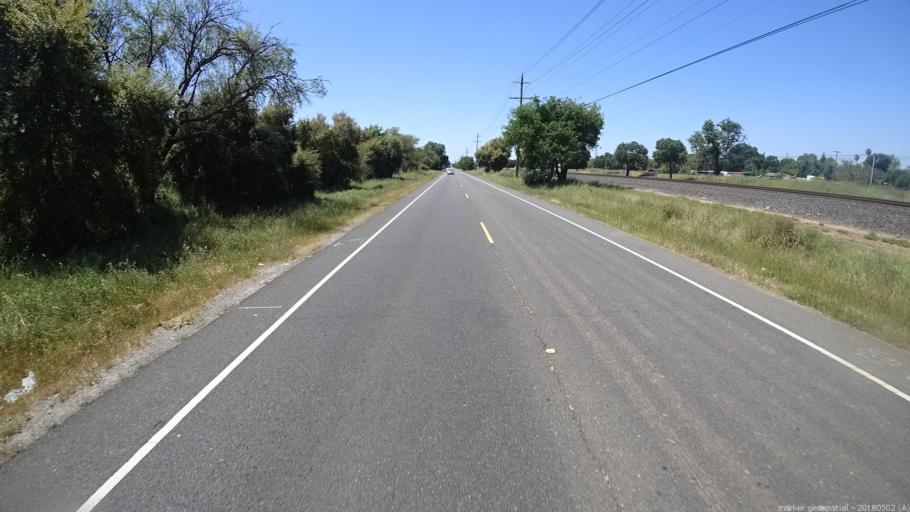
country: US
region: California
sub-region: Sacramento County
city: Arden-Arcade
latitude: 38.6289
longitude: -121.4155
